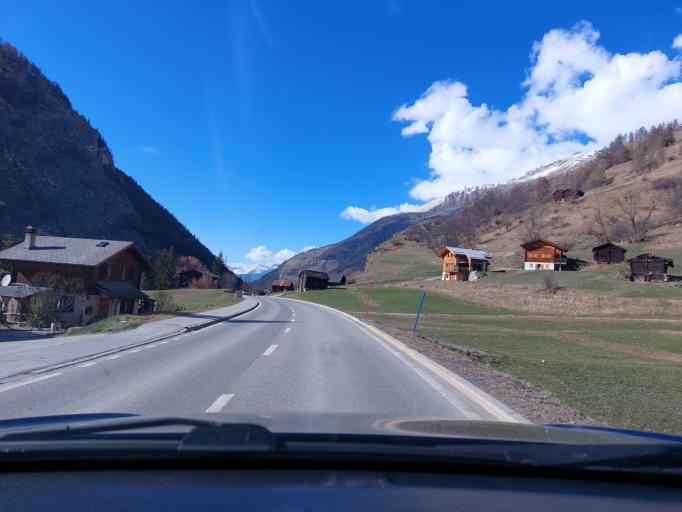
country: CH
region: Valais
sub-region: Herens District
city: Evolene
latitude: 46.0922
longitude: 7.5081
